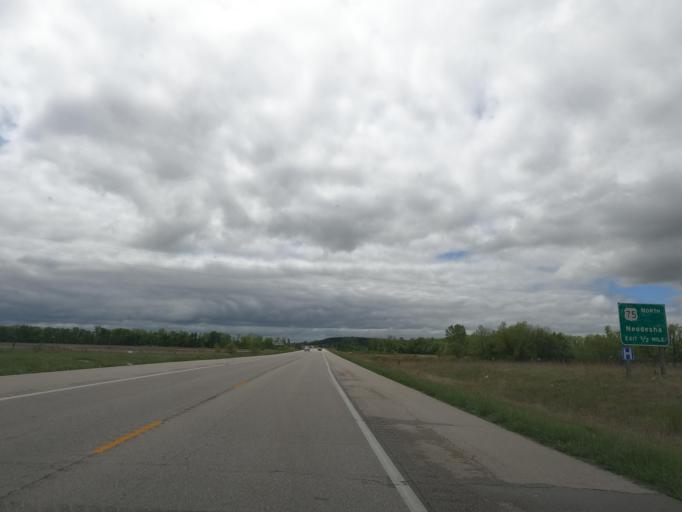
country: US
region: Kansas
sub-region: Wilson County
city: Neodesha
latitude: 37.4288
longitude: -95.7071
